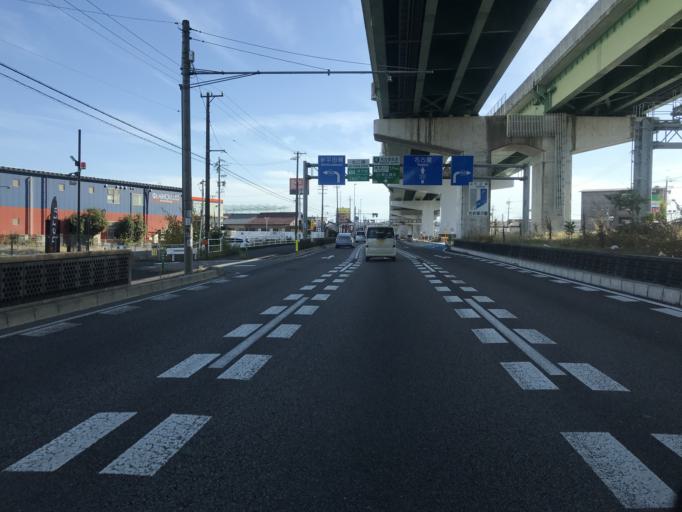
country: JP
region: Aichi
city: Iwakura
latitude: 35.2323
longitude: 136.8509
